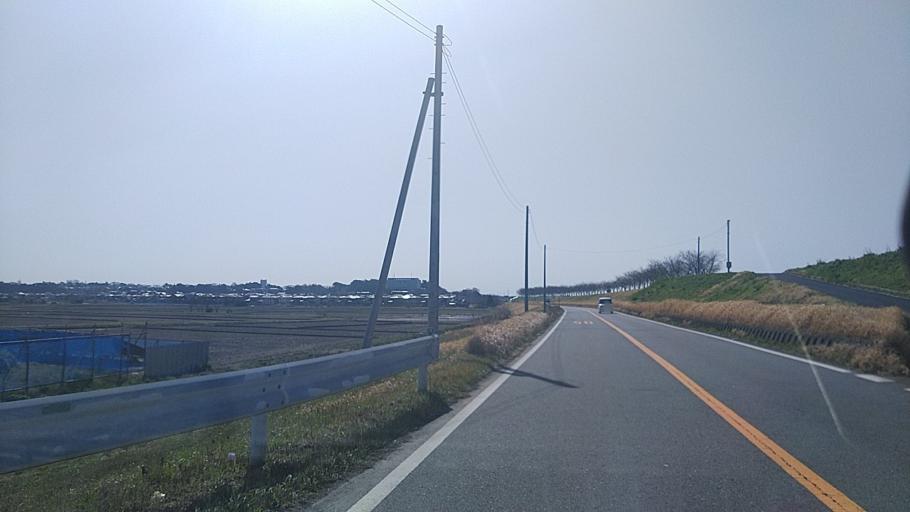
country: JP
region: Ibaraki
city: Fujishiro
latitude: 35.8656
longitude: 140.1323
